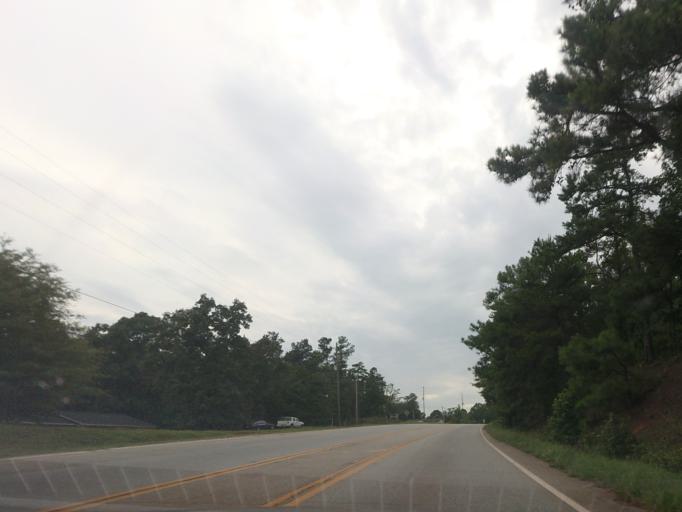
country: US
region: Georgia
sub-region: Twiggs County
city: Jeffersonville
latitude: 32.7660
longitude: -83.4799
